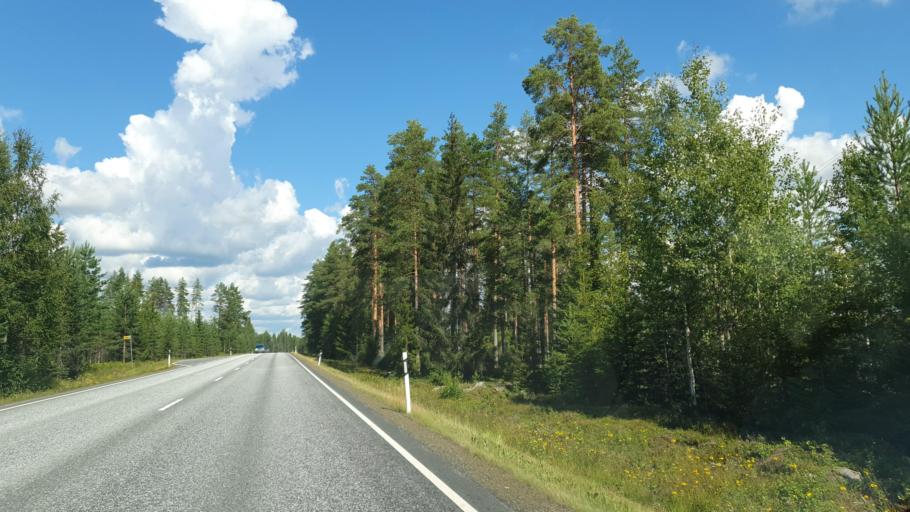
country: FI
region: Northern Savo
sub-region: Ylae-Savo
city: Sonkajaervi
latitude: 63.8273
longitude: 27.4211
